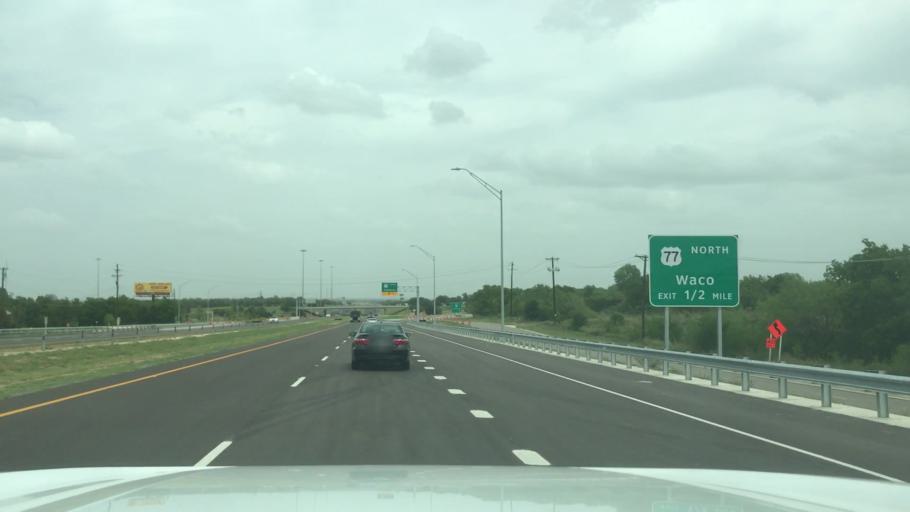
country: US
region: Texas
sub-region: McLennan County
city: Beverly
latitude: 31.4955
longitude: -97.1314
